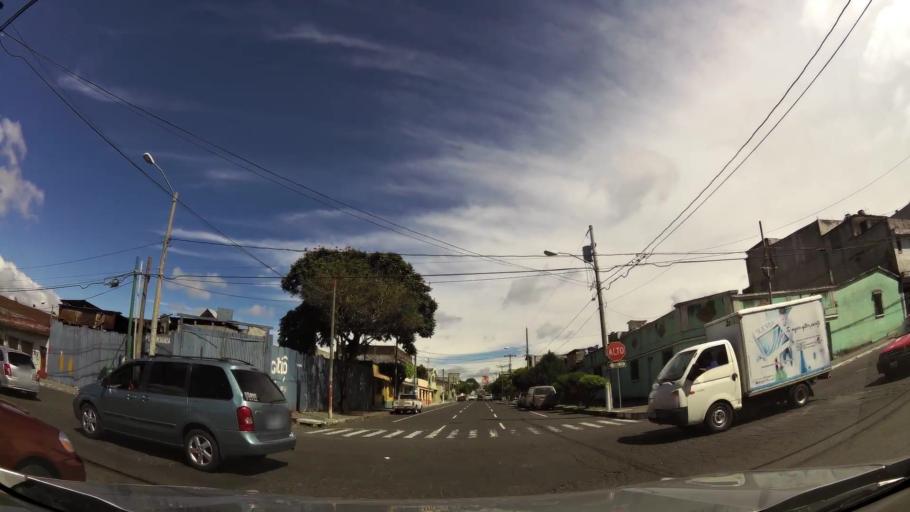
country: GT
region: Guatemala
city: Guatemala City
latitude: 14.5998
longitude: -90.5441
